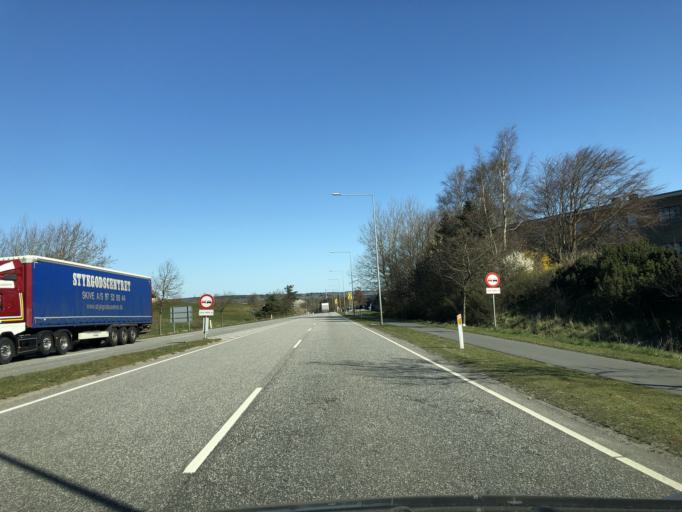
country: DK
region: North Denmark
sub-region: Rebild Kommune
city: Stovring
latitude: 56.8727
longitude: 9.8385
